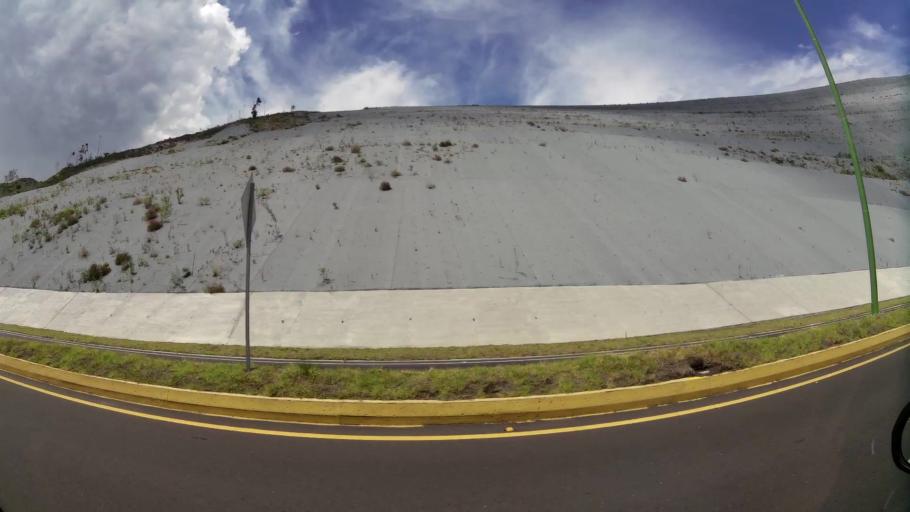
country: EC
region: Pichincha
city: Quito
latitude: -0.1035
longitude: -78.3753
